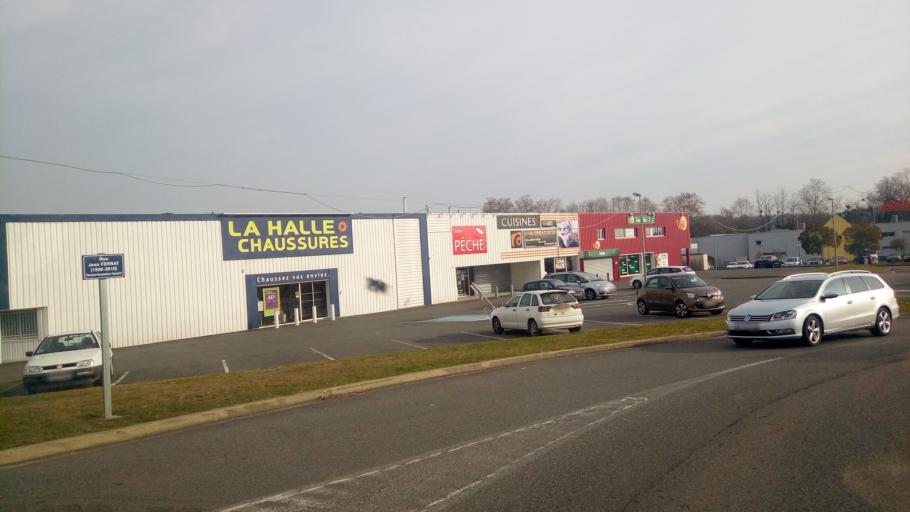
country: FR
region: Aquitaine
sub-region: Departement des Pyrenees-Atlantiques
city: Orthez
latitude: 43.4819
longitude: -0.7476
